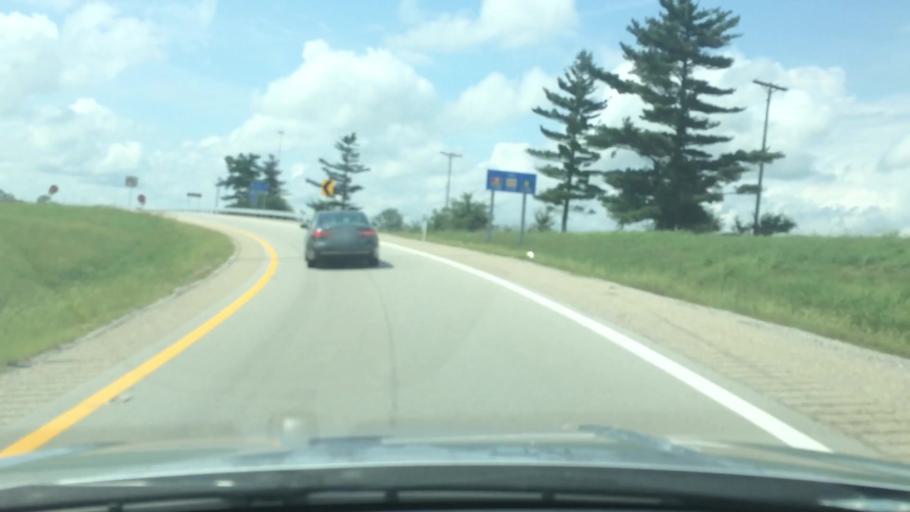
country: US
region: Kentucky
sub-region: Franklin County
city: Frankfort
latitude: 38.1599
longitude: -84.8919
